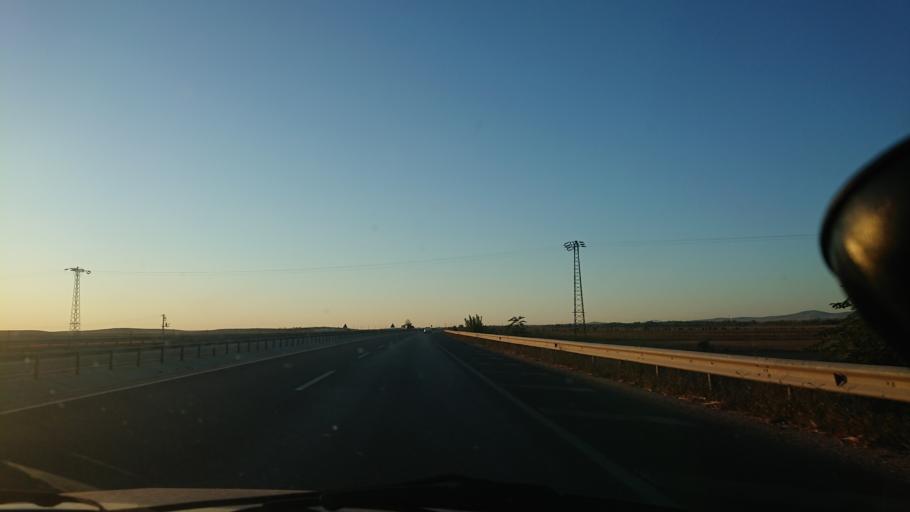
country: TR
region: Eskisehir
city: Mahmudiye
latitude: 39.5428
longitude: 30.9361
